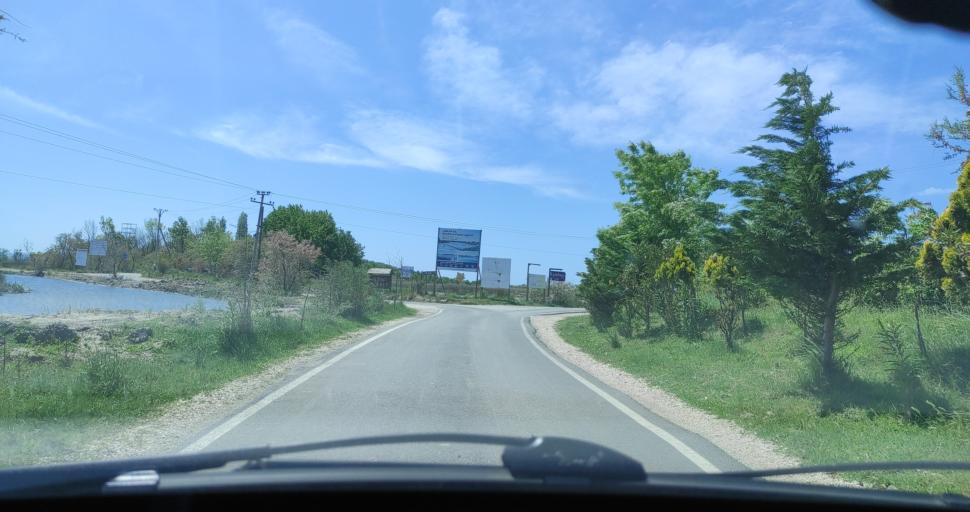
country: AL
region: Lezhe
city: Lezhe
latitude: 41.7536
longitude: 19.6079
